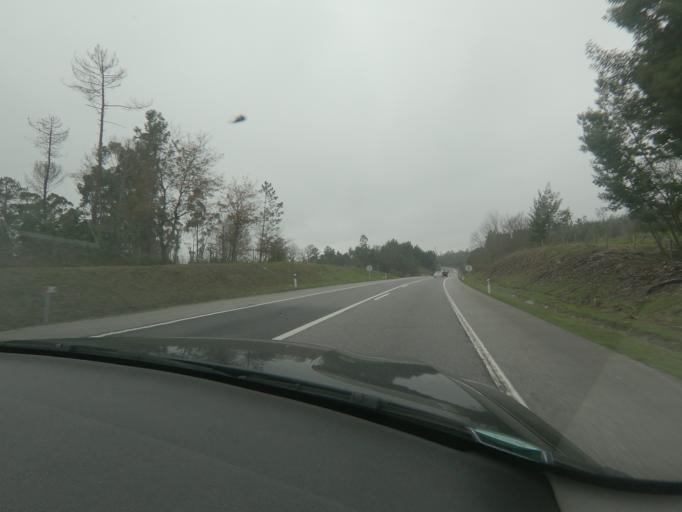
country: PT
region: Viseu
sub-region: Concelho de Tondela
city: Tondela
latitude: 40.5683
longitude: -8.0396
